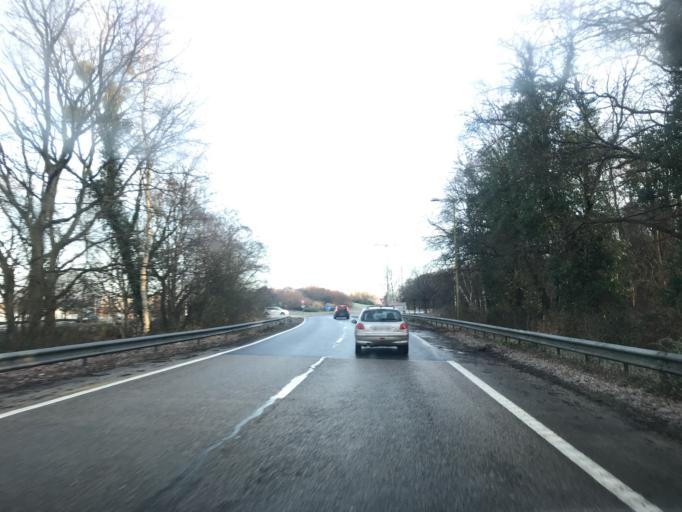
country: FR
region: Haute-Normandie
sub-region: Departement de la Seine-Maritime
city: Le Grand-Quevilly
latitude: 49.3876
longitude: 1.0557
